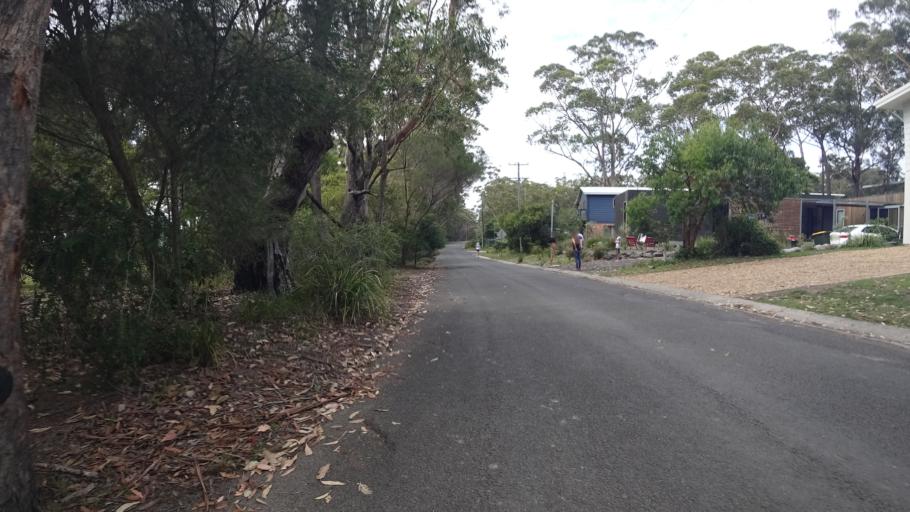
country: AU
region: New South Wales
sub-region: Shoalhaven Shire
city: Milton
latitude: -35.2357
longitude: 150.5289
